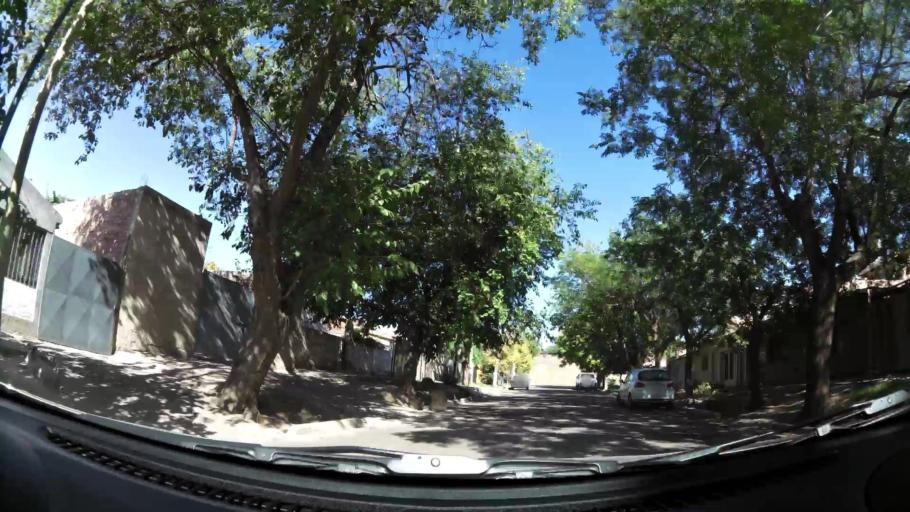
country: AR
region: Mendoza
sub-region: Departamento de Godoy Cruz
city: Godoy Cruz
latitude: -32.9281
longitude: -68.8630
